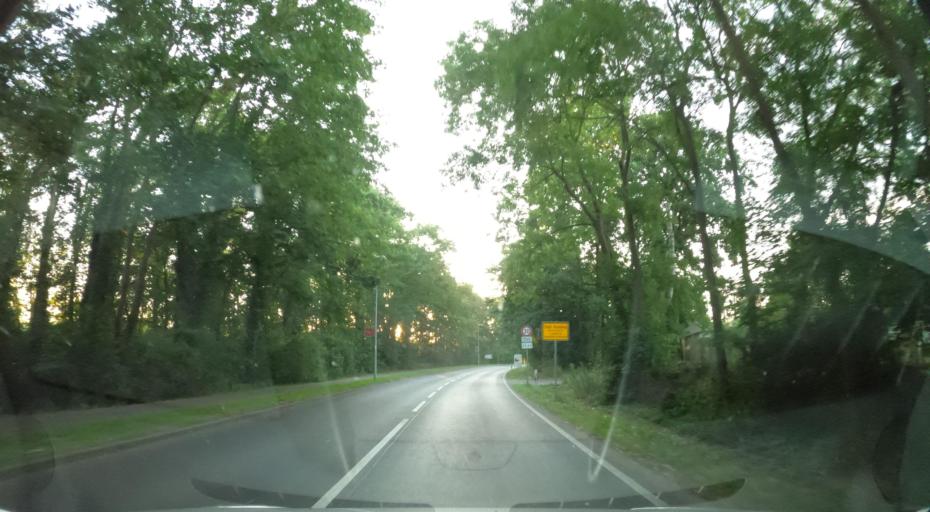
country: DE
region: Mecklenburg-Vorpommern
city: Strasburg
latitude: 53.5029
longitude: 13.7553
